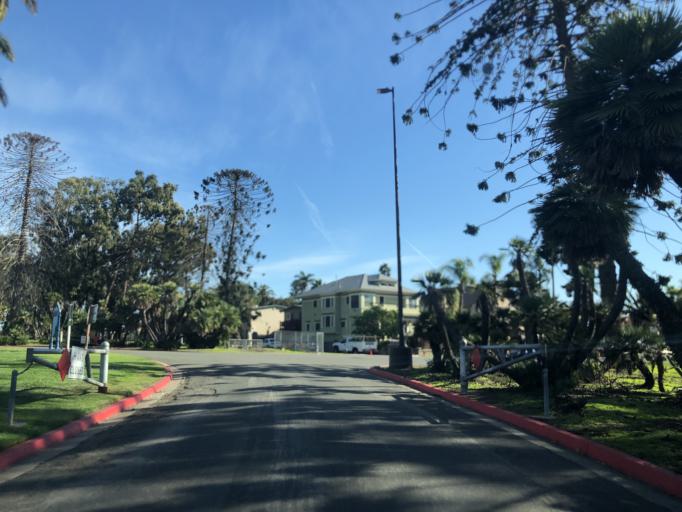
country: US
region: California
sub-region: San Diego County
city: San Diego
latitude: 32.7199
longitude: -117.1407
